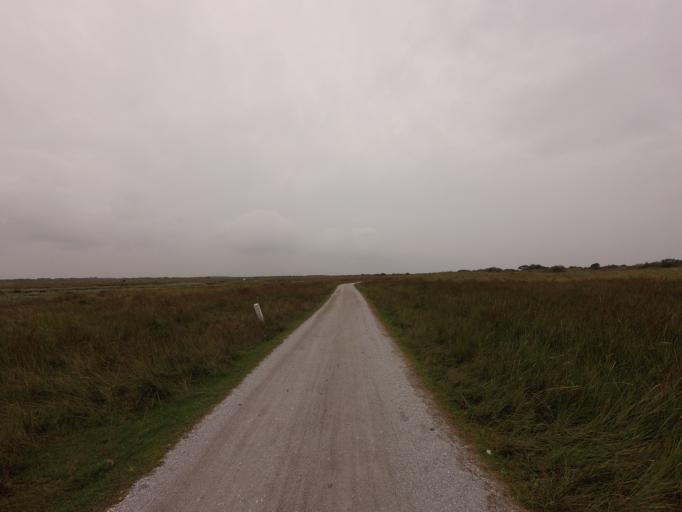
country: NL
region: Friesland
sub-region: Gemeente Schiermonnikoog
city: Schiermonnikoog
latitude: 53.4868
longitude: 6.2131
